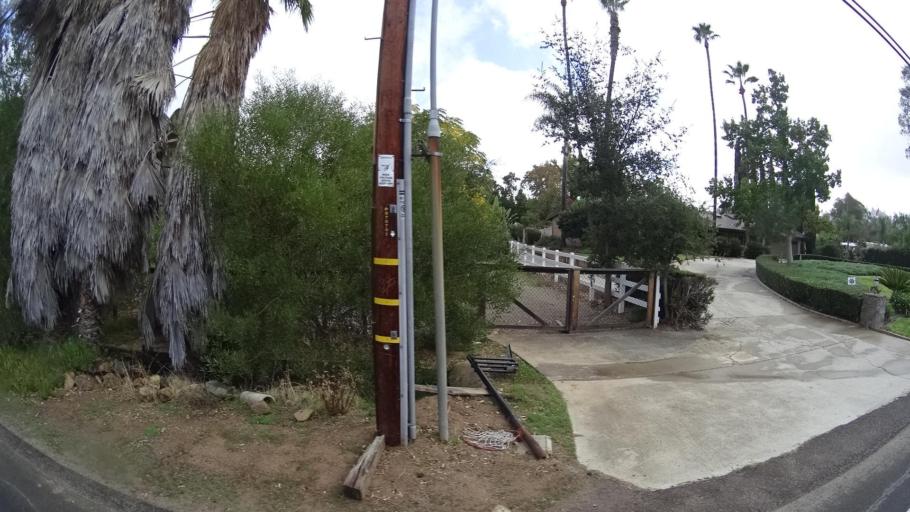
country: US
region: California
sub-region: San Diego County
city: Granite Hills
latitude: 32.7853
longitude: -116.9062
